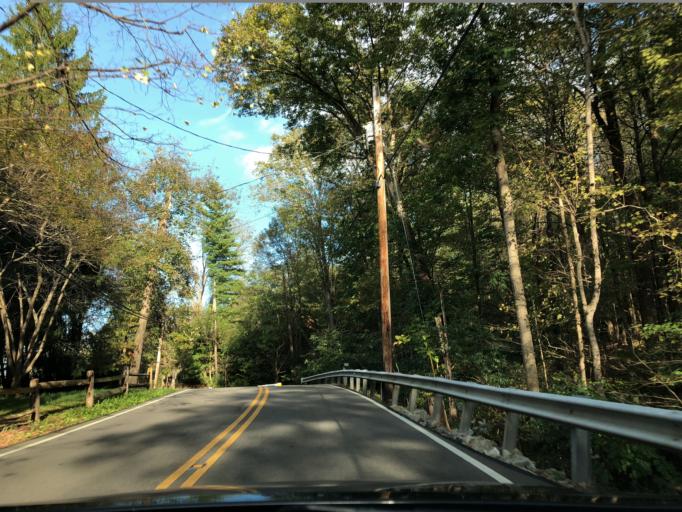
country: US
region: Ohio
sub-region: Hamilton County
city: The Village of Indian Hill
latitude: 39.2490
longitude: -84.2852
